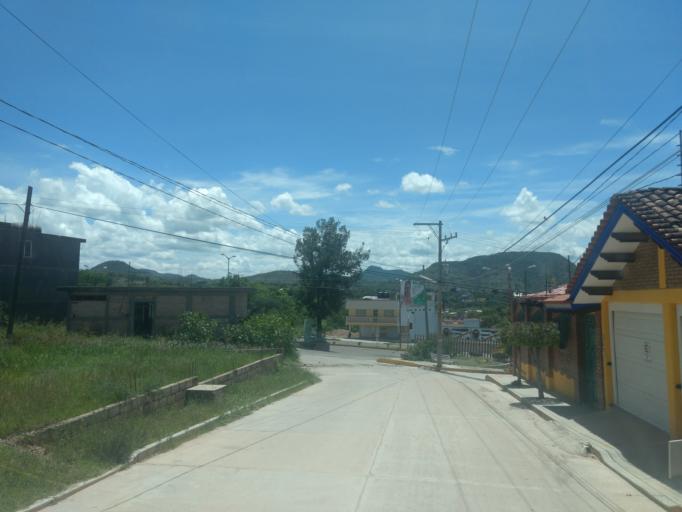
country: MX
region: Oaxaca
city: Ciudad de Huajuapam de Leon
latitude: 17.8179
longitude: -97.7920
